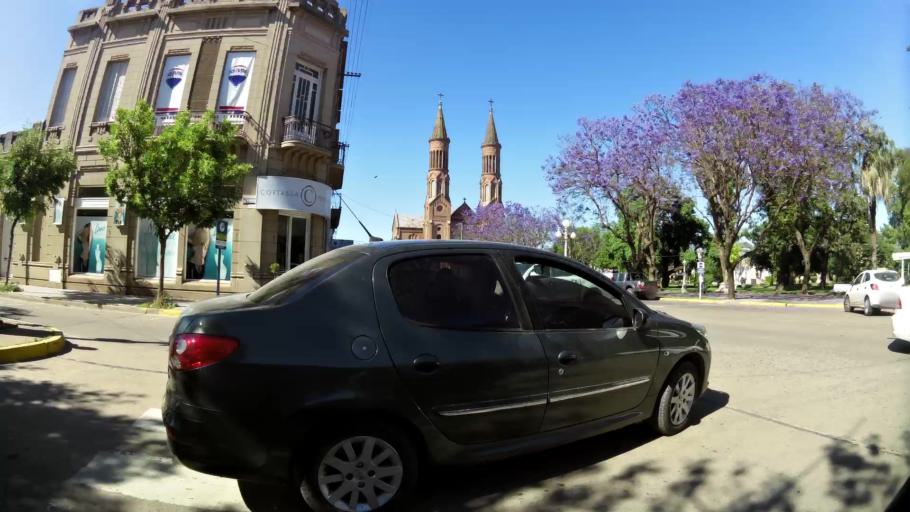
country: AR
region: Santa Fe
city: Esperanza
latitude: -31.4492
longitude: -60.9293
